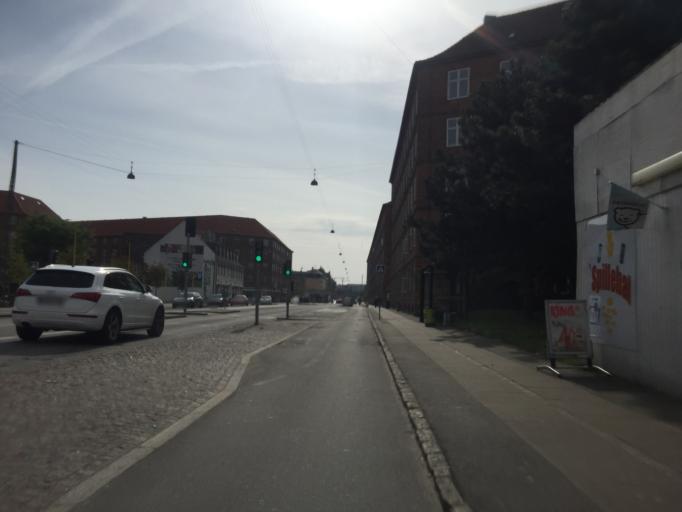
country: DK
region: Capital Region
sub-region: Kobenhavn
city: Vanlose
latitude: 55.6677
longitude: 12.5000
